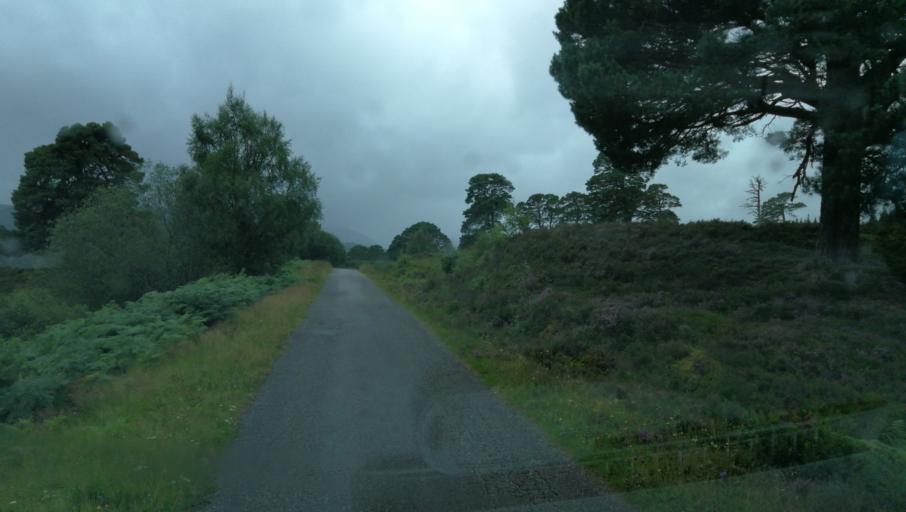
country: GB
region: Scotland
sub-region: Highland
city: Spean Bridge
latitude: 57.2701
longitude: -4.9669
